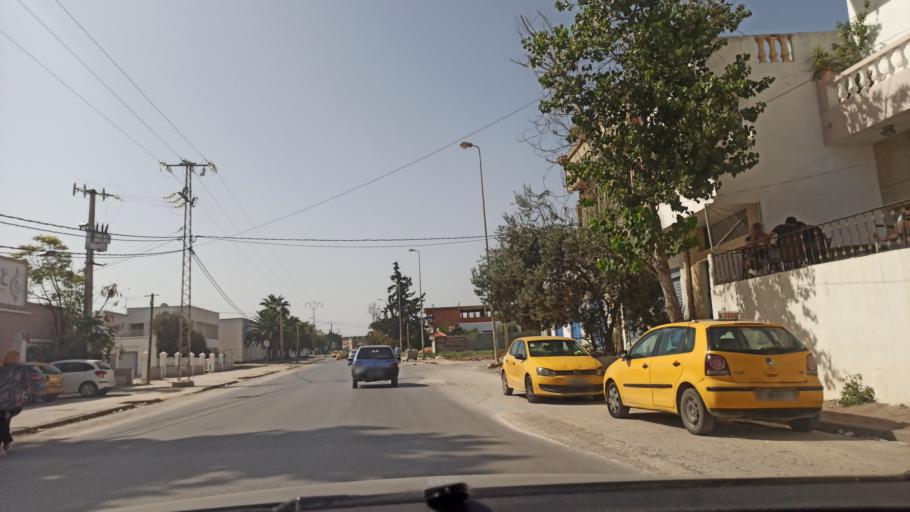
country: TN
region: Manouba
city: Manouba
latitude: 36.7603
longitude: 10.1068
